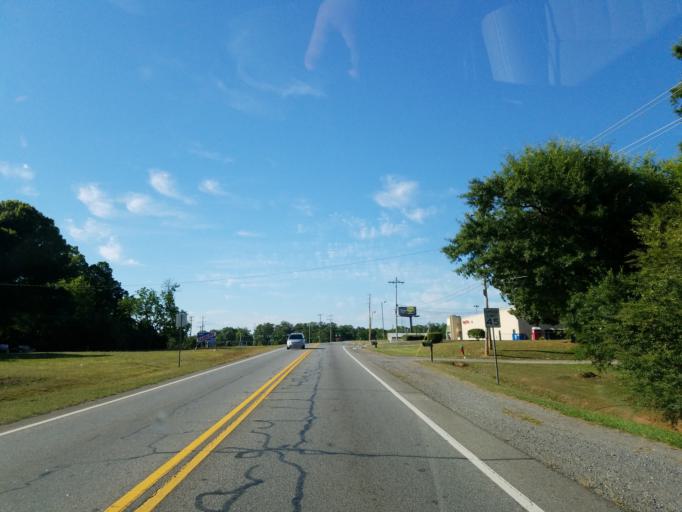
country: US
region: Georgia
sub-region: Gordon County
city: Calhoun
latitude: 34.4758
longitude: -84.9345
